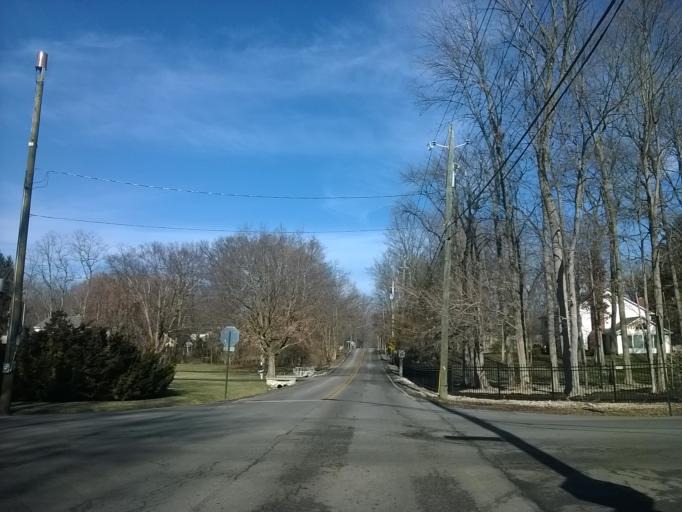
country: US
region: Indiana
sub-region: Marion County
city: Broad Ripple
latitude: 39.8831
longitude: -86.0983
